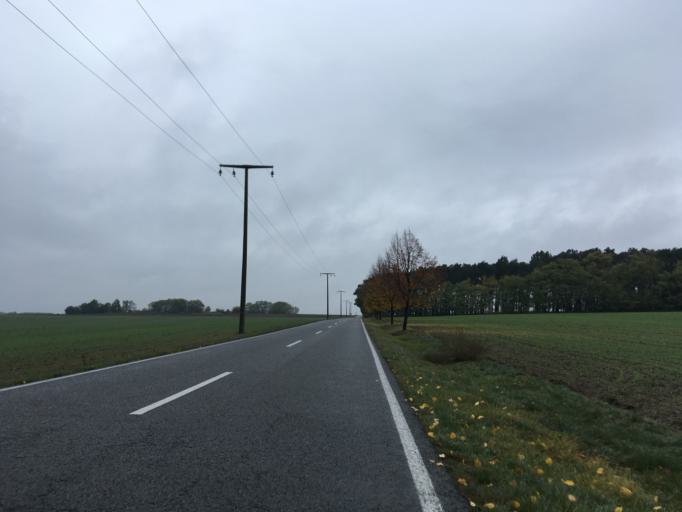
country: DE
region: Brandenburg
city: Friedland
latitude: 52.0630
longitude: 14.1878
